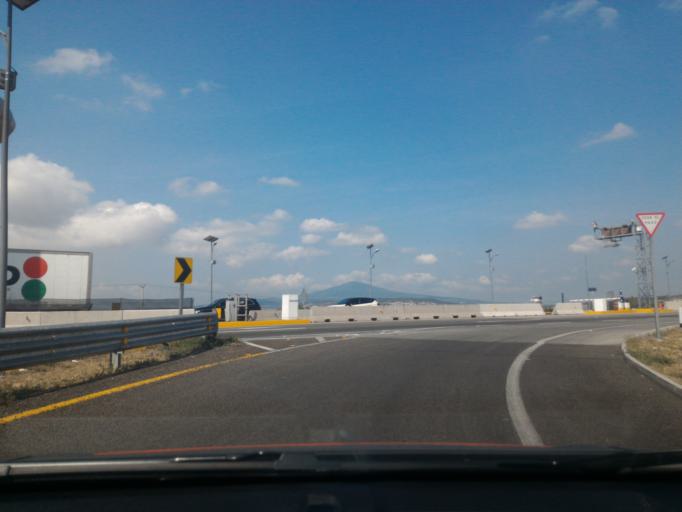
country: MX
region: Guanajuato
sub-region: Penjamo
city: Estacion la Piedad
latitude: 20.3959
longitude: -101.9935
